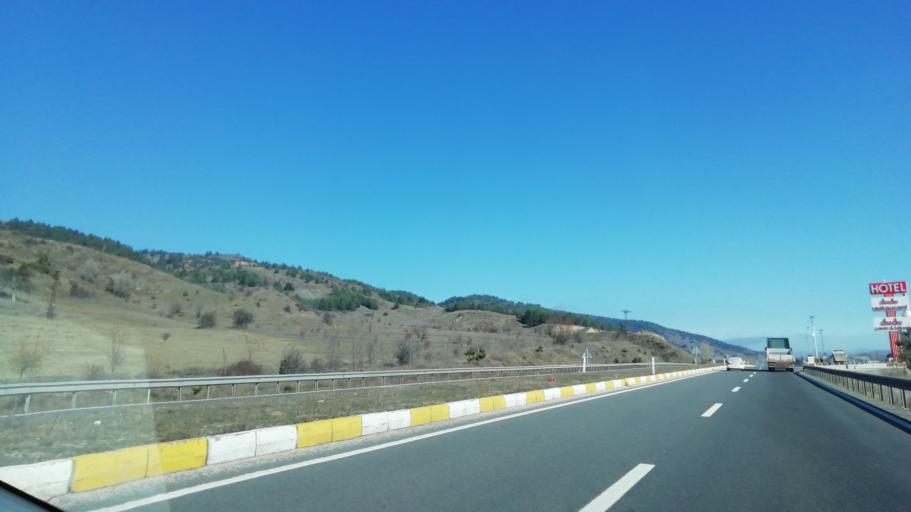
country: TR
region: Karabuk
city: Gozyeri
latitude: 40.8360
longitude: 32.4124
